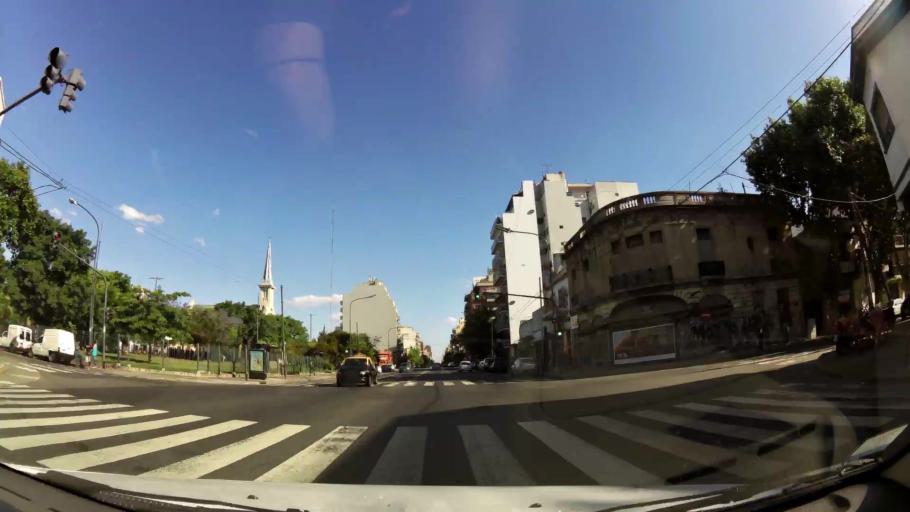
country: AR
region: Buenos Aires F.D.
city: Villa Santa Rita
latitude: -34.6211
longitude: -58.4739
